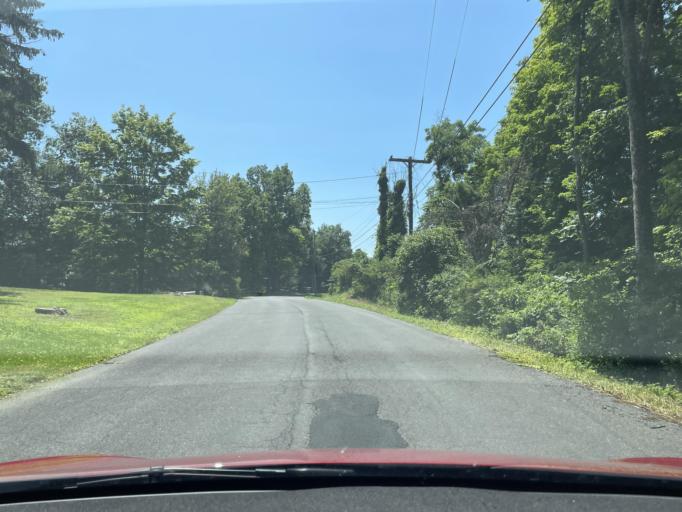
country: US
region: New York
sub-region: Ulster County
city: Lake Katrine
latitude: 42.0098
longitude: -73.9788
